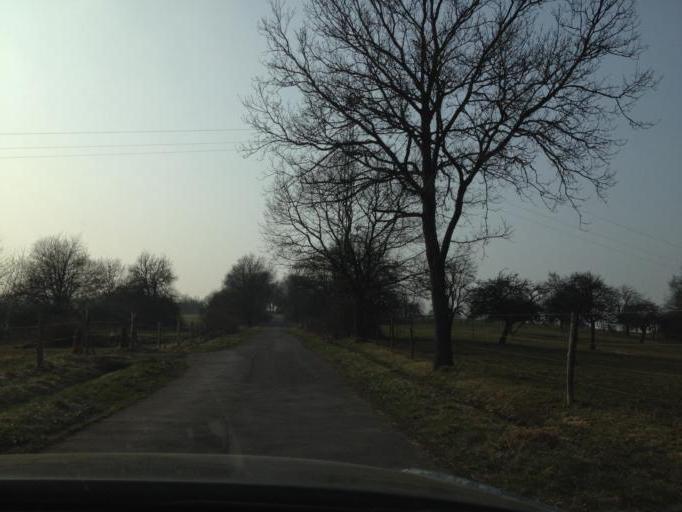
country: DE
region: Saarland
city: Ottweiler
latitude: 49.4302
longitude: 7.1509
